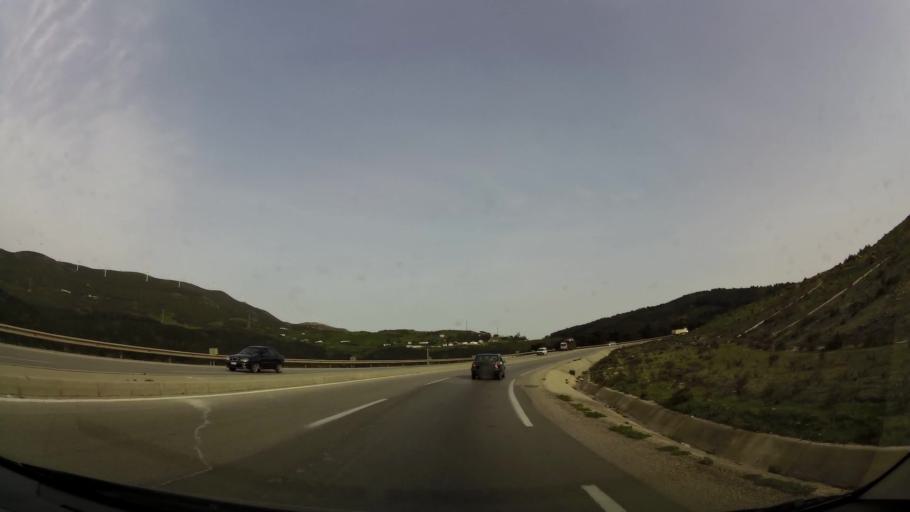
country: MA
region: Tanger-Tetouan
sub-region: Tanger-Assilah
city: Dar Chaoui
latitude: 35.5657
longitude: -5.5858
